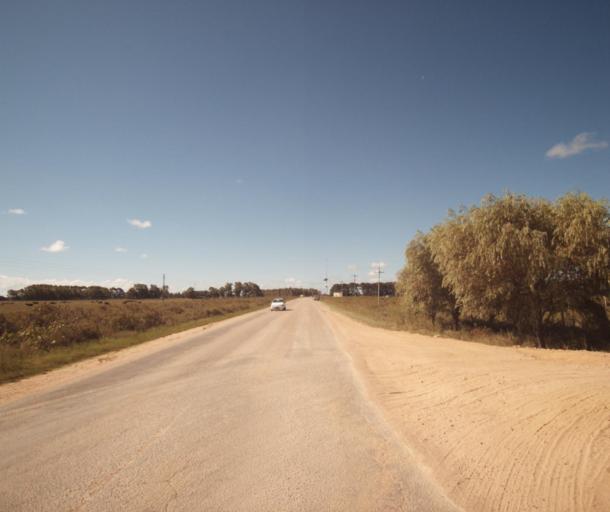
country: BR
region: Rio Grande do Sul
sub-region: Santa Vitoria Do Palmar
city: Santa Vitoria do Palmar
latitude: -33.5625
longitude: -53.3719
